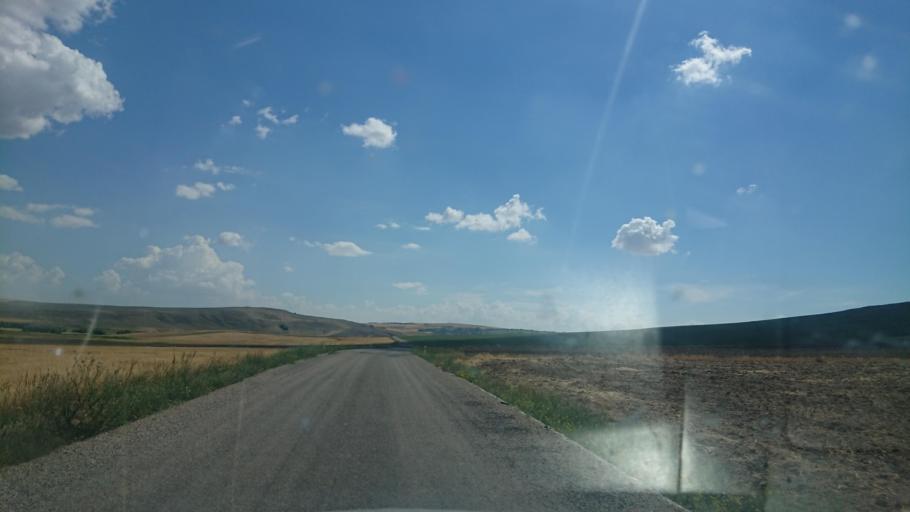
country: TR
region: Aksaray
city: Agacoren
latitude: 38.7927
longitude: 33.8159
